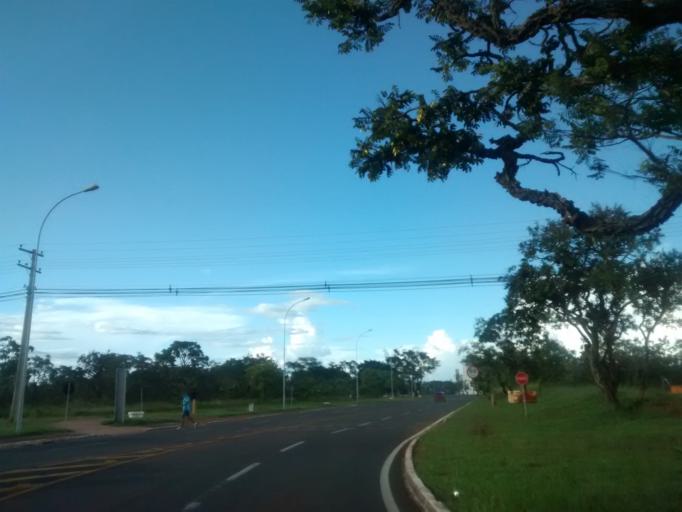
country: BR
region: Federal District
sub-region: Brasilia
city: Brasilia
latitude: -15.7840
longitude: -47.9252
